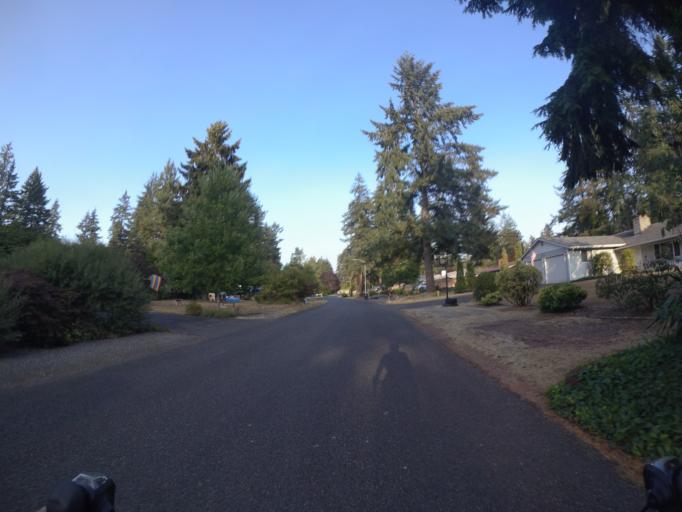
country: US
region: Washington
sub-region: Pierce County
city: Lakewood
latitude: 47.1488
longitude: -122.5184
